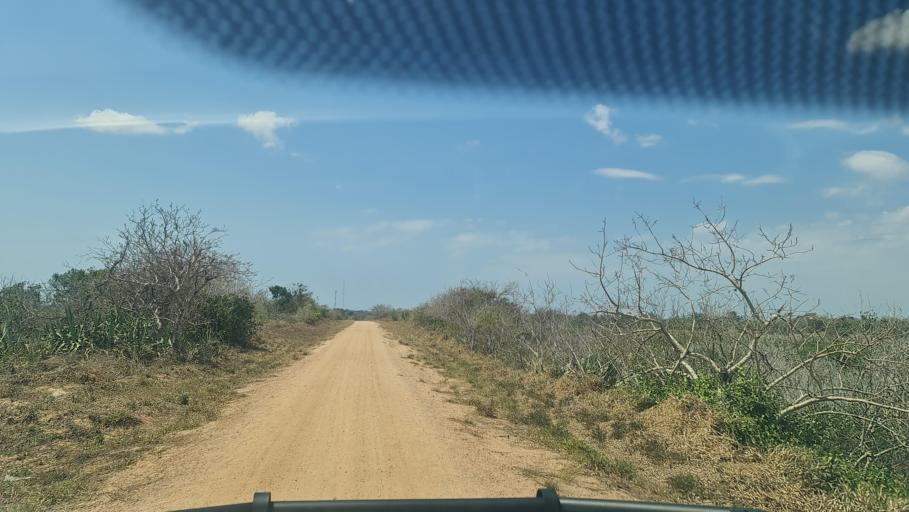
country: MZ
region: Nampula
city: Ilha de Mocambique
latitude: -15.1859
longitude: 40.5181
